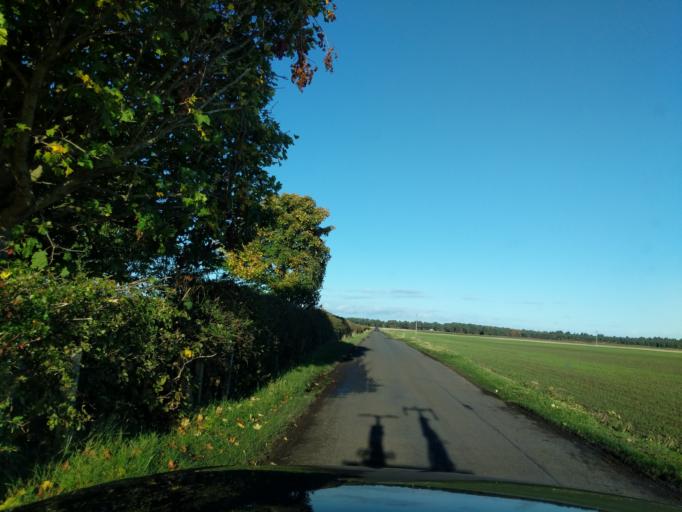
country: GB
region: Scotland
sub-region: Fife
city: Leuchars
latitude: 56.3944
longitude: -2.8699
